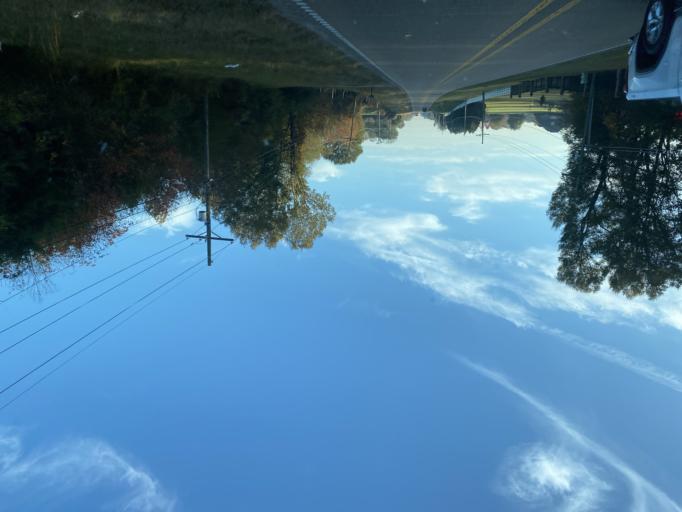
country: US
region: Mississippi
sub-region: Madison County
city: Madison
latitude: 32.5067
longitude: -90.0881
